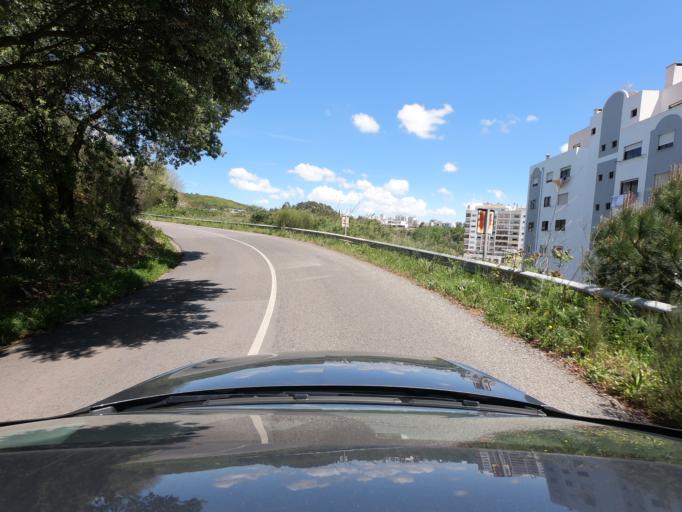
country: PT
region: Lisbon
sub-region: Oeiras
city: Carnaxide
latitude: 38.7286
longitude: -9.2388
